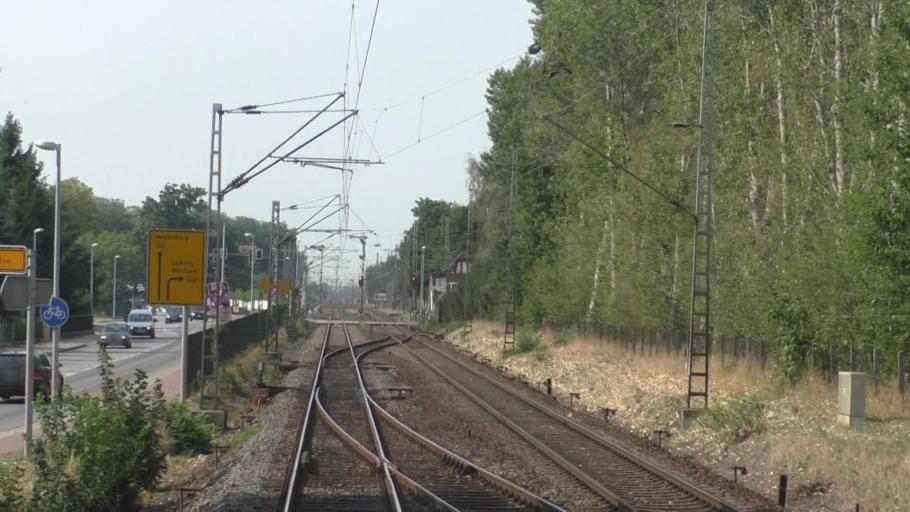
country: DE
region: Saxony-Anhalt
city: Wahlitz
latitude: 52.1315
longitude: 11.7594
